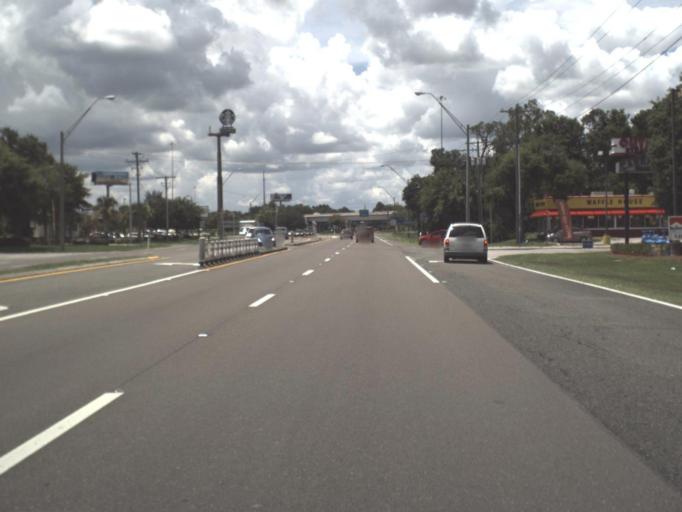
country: US
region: Florida
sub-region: Hillsborough County
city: Plant City
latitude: 28.0251
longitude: -82.1493
